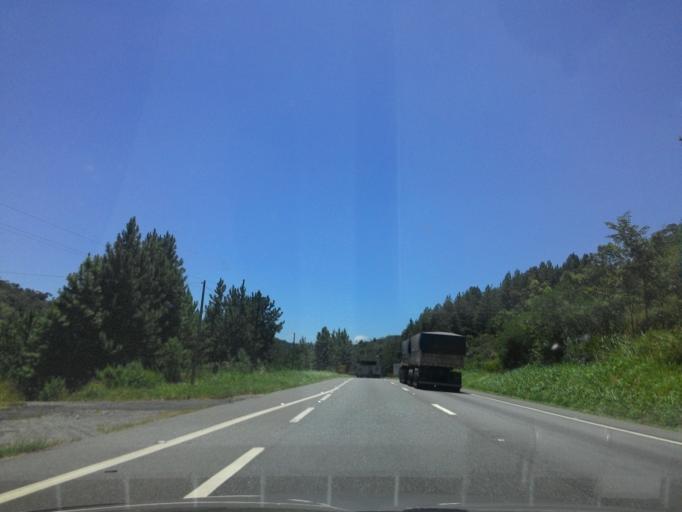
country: BR
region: Sao Paulo
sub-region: Cajati
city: Cajati
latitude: -24.9863
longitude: -48.5056
